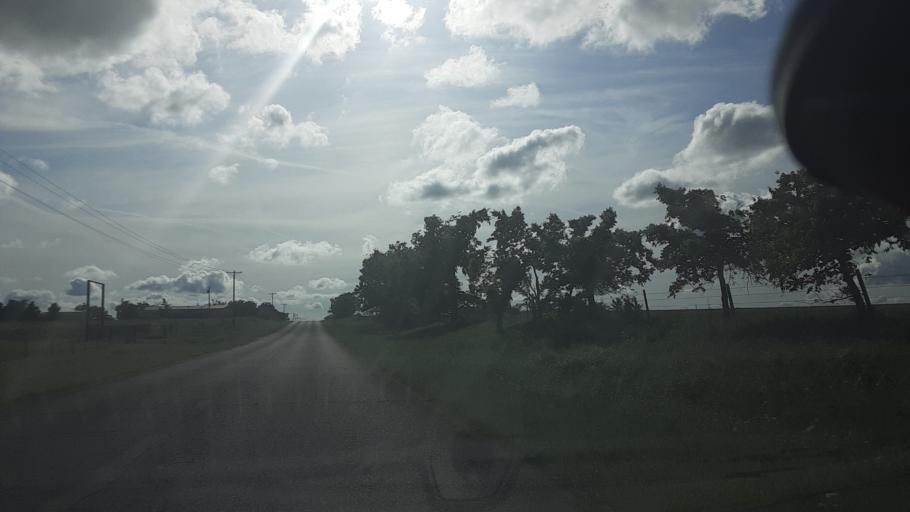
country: US
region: Oklahoma
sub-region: Logan County
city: Langston
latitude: 36.0579
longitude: -97.3735
